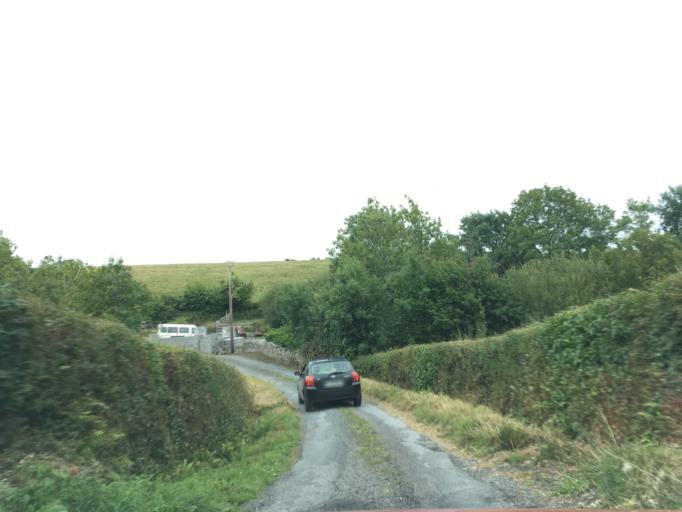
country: IE
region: Munster
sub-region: County Limerick
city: Askeaton
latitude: 52.7172
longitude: -9.0633
